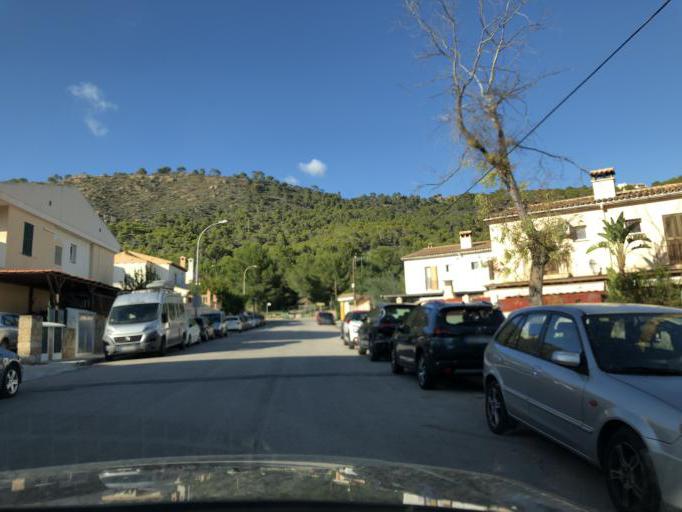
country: ES
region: Balearic Islands
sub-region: Illes Balears
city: Camp de Mar
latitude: 39.5394
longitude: 2.4393
